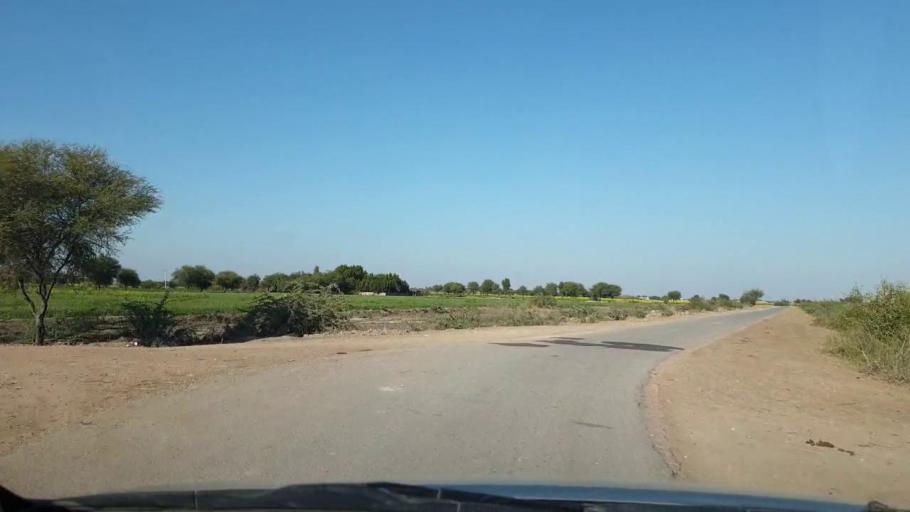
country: PK
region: Sindh
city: Jhol
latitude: 25.8263
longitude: 68.9484
